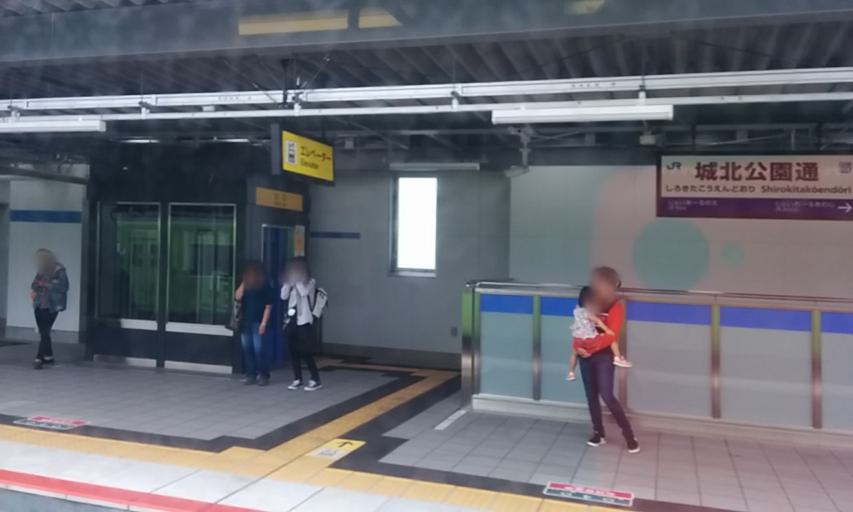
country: JP
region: Osaka
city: Moriguchi
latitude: 34.7236
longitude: 135.5306
